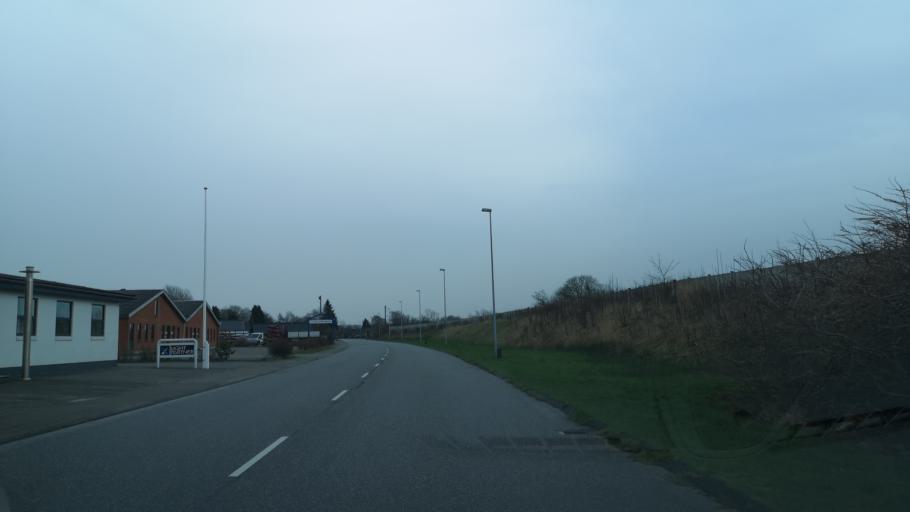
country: DK
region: Central Jutland
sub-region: Herning Kommune
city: Lind
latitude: 56.1122
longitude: 8.9689
